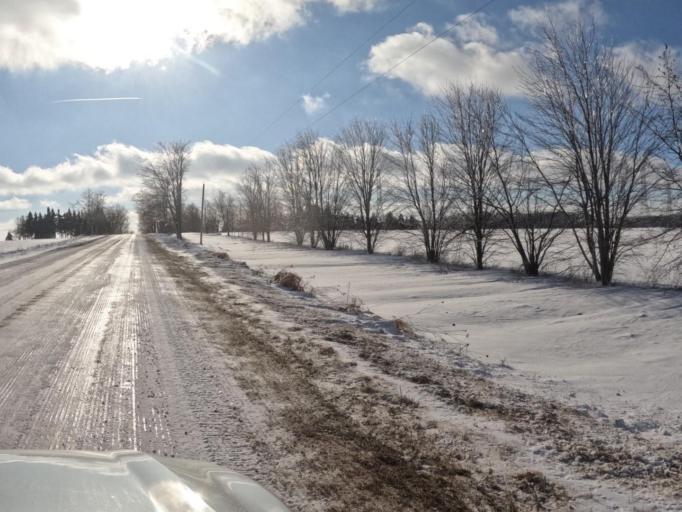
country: CA
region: Ontario
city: Shelburne
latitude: 43.9992
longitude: -80.4093
